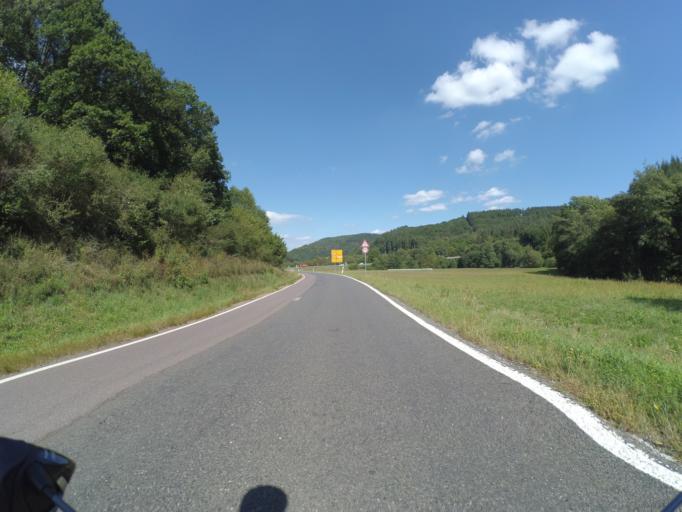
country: DE
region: Rheinland-Pfalz
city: Breit
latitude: 49.7706
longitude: 6.8922
